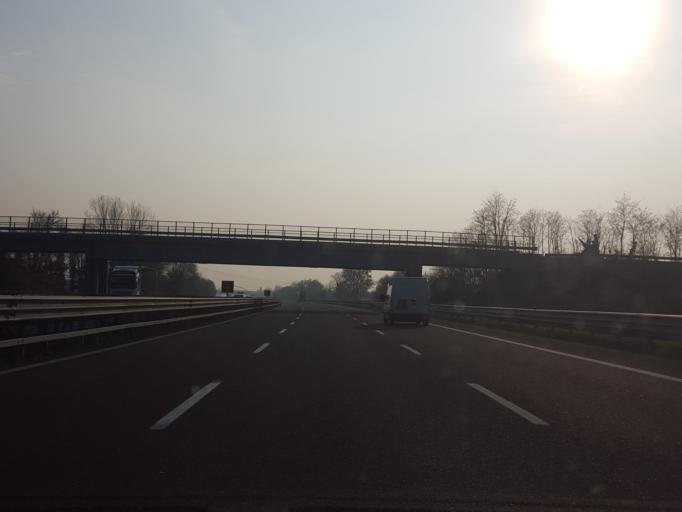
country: IT
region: Veneto
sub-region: Provincia di Treviso
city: Conscio
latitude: 45.6143
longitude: 12.2993
